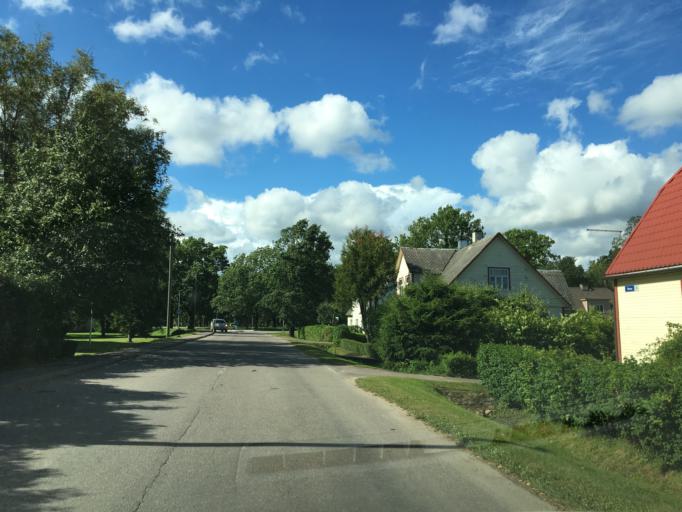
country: EE
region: Paernumaa
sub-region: Vaendra vald (alev)
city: Vandra
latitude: 58.6501
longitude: 25.0281
